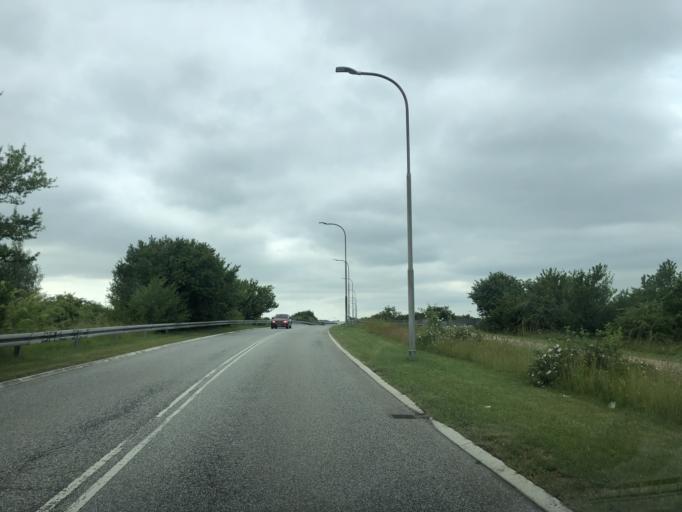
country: DK
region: Capital Region
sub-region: Ishoj Kommune
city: Ishoj
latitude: 55.6024
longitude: 12.3439
